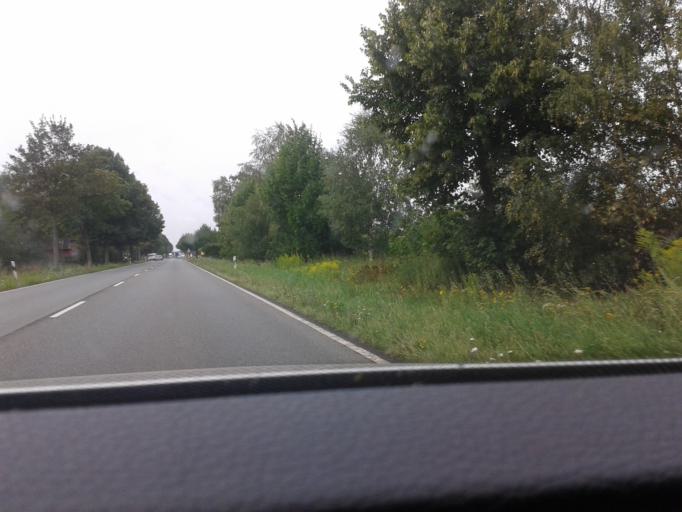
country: DE
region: Lower Saxony
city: Tappenbeck
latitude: 52.4620
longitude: 10.7319
